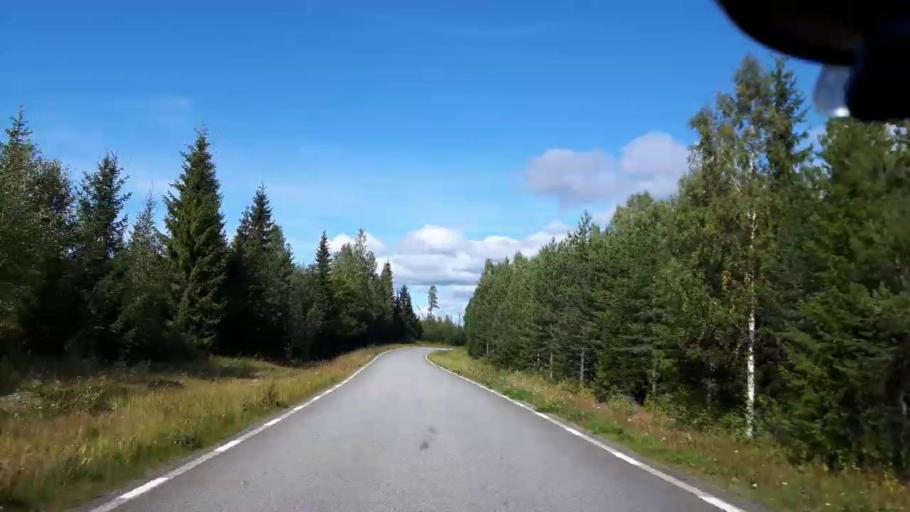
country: SE
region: Jaemtland
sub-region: OEstersunds Kommun
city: Brunflo
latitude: 63.2148
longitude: 15.2461
